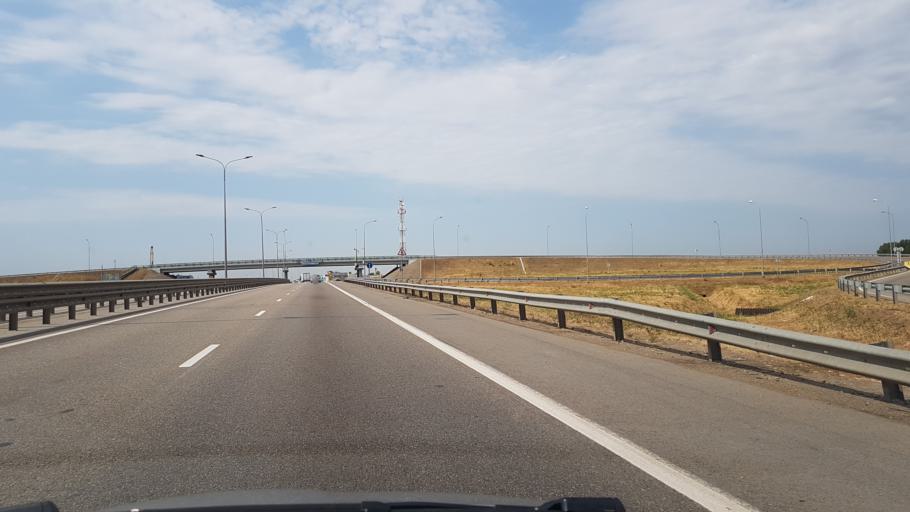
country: RU
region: Krasnodarskiy
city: Plastunovskaya
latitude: 45.3106
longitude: 39.2389
